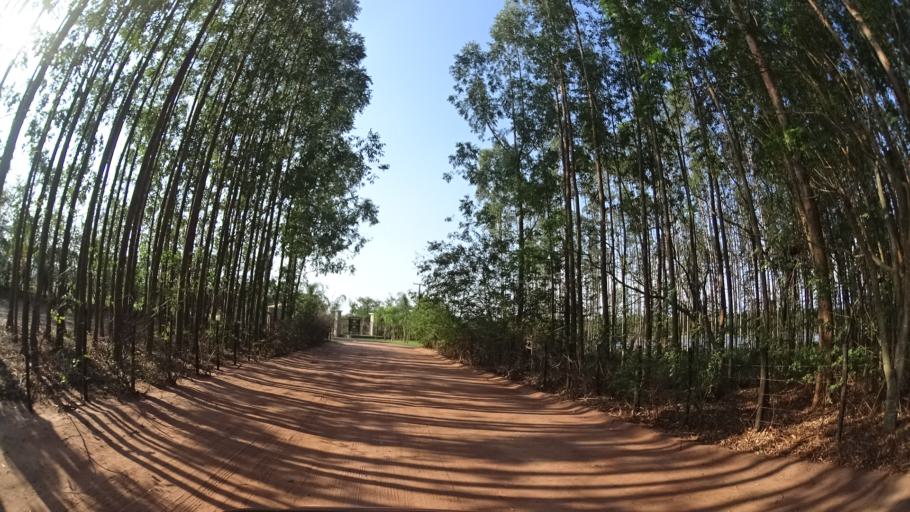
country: BR
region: Sao Paulo
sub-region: Urupes
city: Urupes
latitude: -21.4054
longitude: -49.5311
